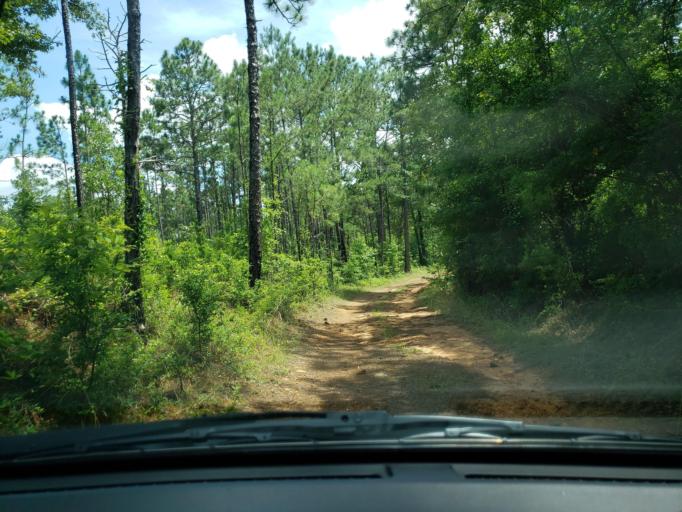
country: US
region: Alabama
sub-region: Elmore County
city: Eclectic
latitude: 32.6319
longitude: -85.9433
